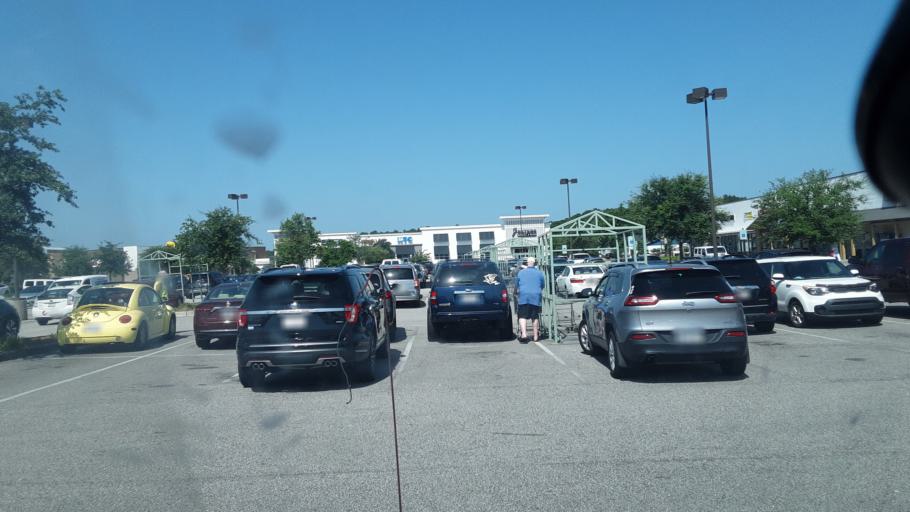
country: US
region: South Carolina
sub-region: Horry County
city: Myrtle Beach
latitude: 33.7591
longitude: -78.8550
